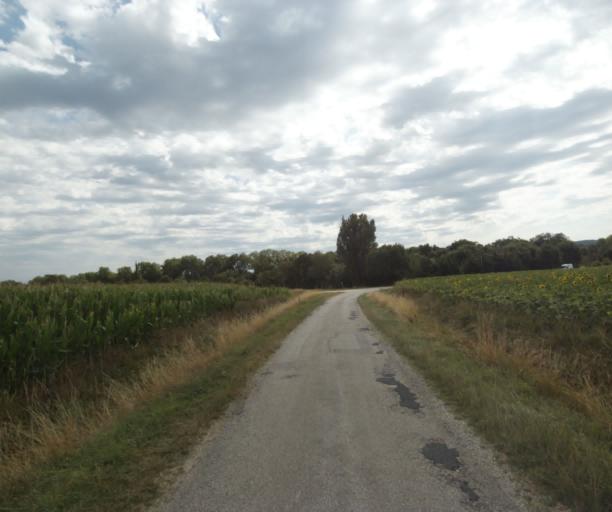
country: FR
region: Midi-Pyrenees
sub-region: Departement de la Haute-Garonne
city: Revel
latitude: 43.4318
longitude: 1.9497
